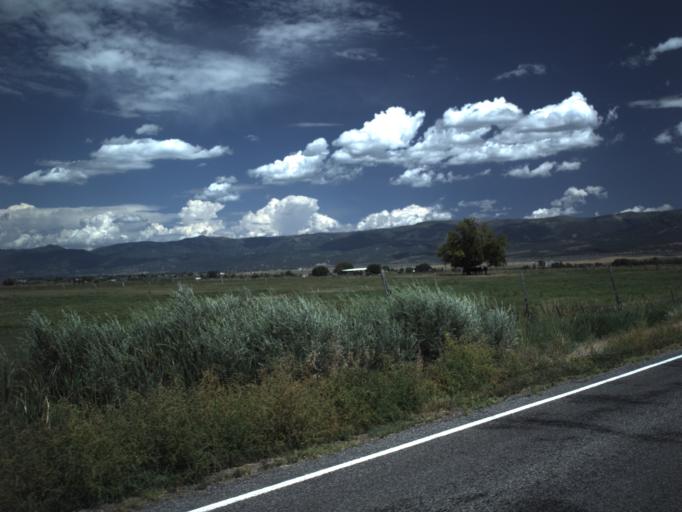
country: US
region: Utah
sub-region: Sanpete County
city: Moroni
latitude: 39.4810
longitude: -111.5247
